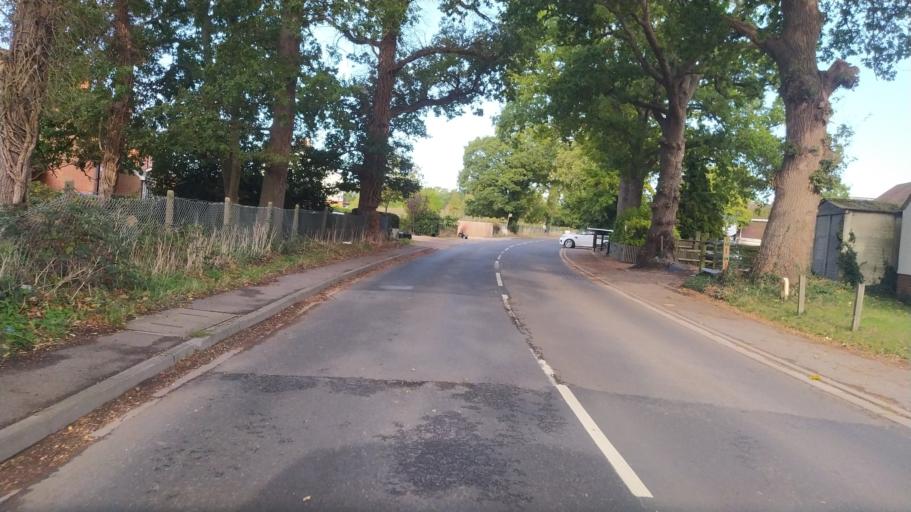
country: GB
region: England
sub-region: Hampshire
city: Eversley
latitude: 51.3587
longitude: -0.8935
